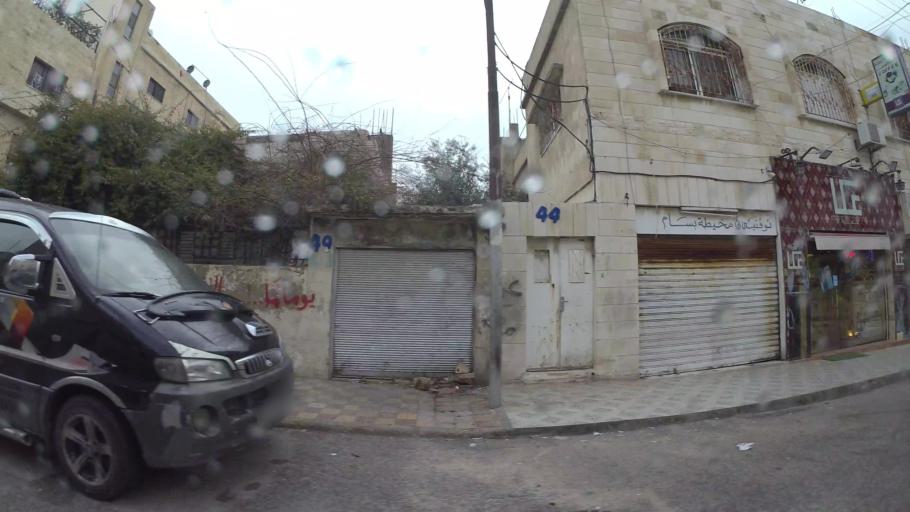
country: JO
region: Amman
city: Amman
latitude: 31.9601
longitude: 35.9374
